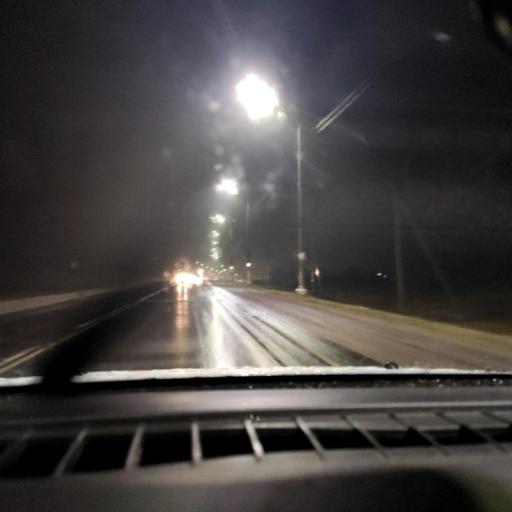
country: RU
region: Voronezj
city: Devitsa
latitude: 51.6319
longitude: 38.9824
